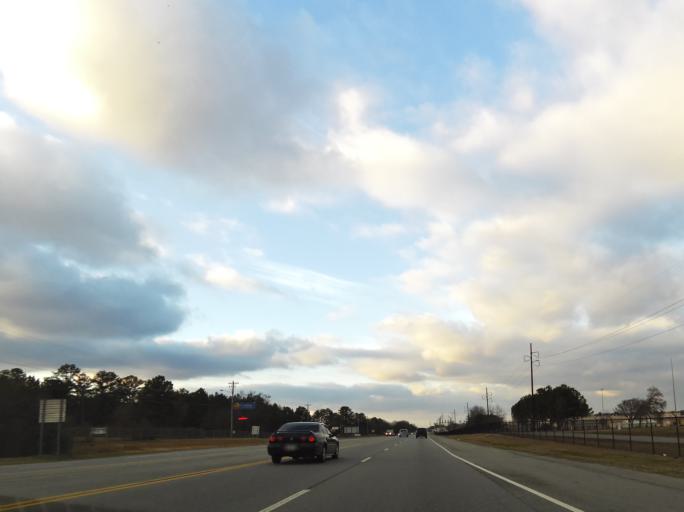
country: US
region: Georgia
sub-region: Houston County
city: Robins Air Force Base
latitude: 32.5959
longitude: -83.5917
